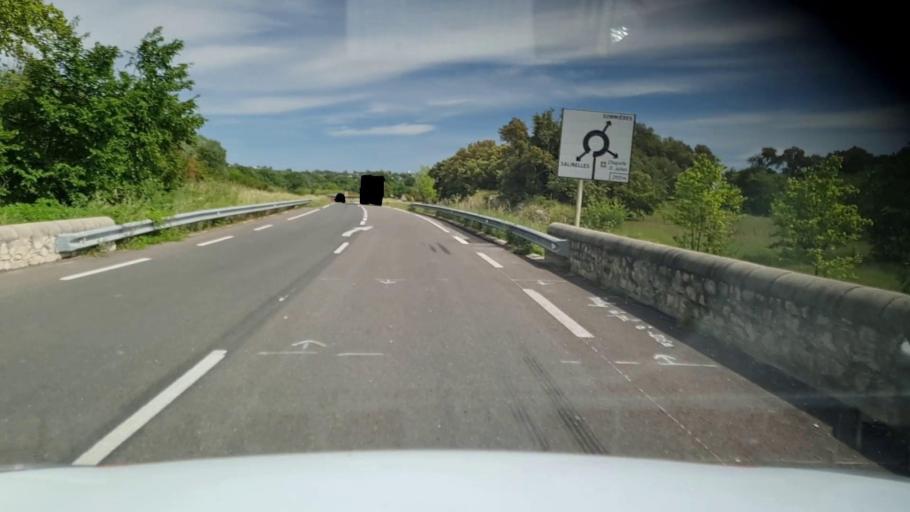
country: FR
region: Languedoc-Roussillon
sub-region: Departement du Gard
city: Sommieres
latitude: 43.8039
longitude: 4.0694
